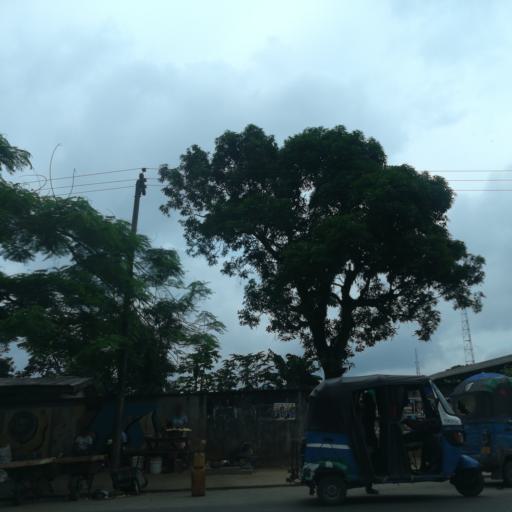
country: NG
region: Rivers
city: Port Harcourt
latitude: 4.8110
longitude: 7.0456
